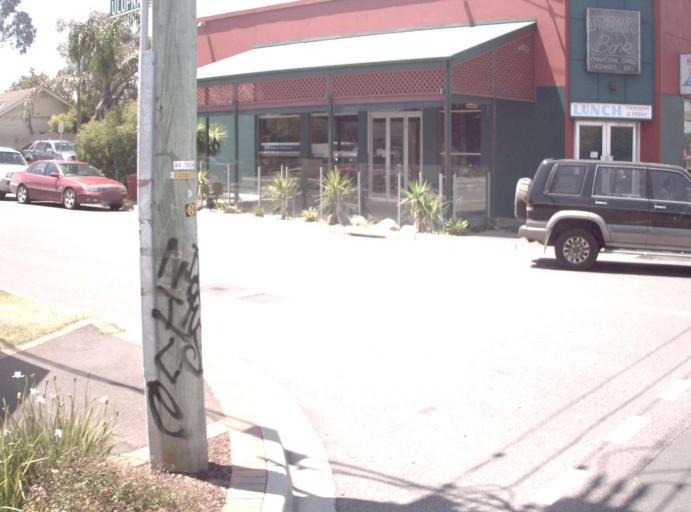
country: AU
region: Victoria
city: Ormond
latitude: -37.9042
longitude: 145.0424
